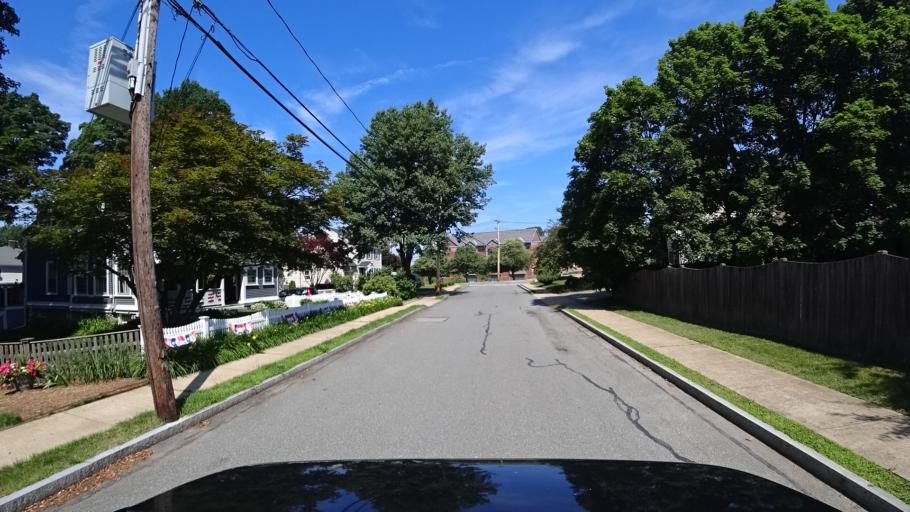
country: US
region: Massachusetts
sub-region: Norfolk County
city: Dedham
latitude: 42.2433
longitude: -71.1661
